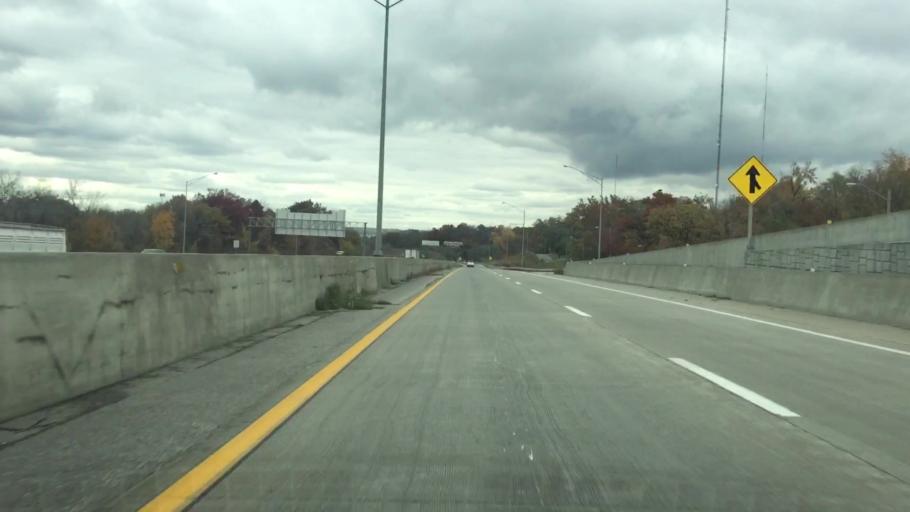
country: US
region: Missouri
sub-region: Jackson County
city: Sugar Creek
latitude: 39.0664
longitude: -94.4878
